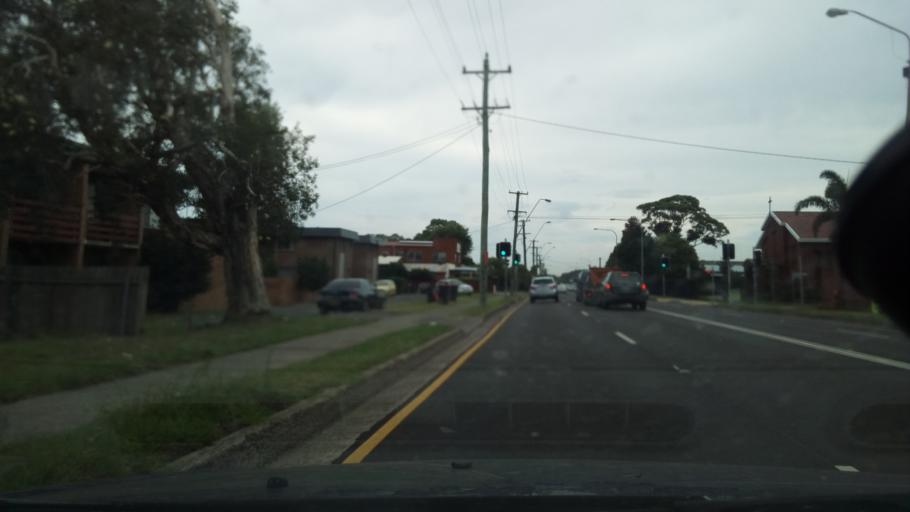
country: AU
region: New South Wales
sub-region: Wollongong
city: Fairy Meadow
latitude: -34.3970
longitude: 150.8925
